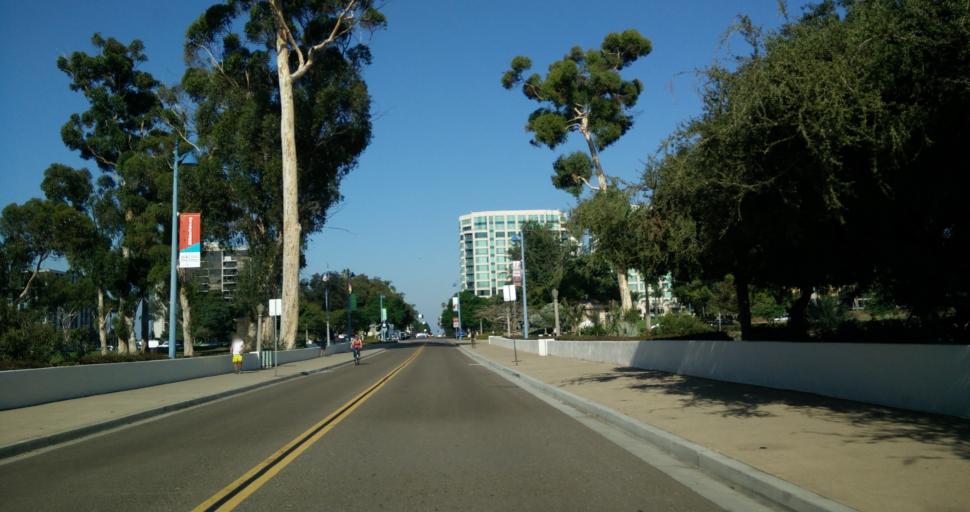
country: US
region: California
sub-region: San Diego County
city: San Diego
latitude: 32.7314
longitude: -117.1565
